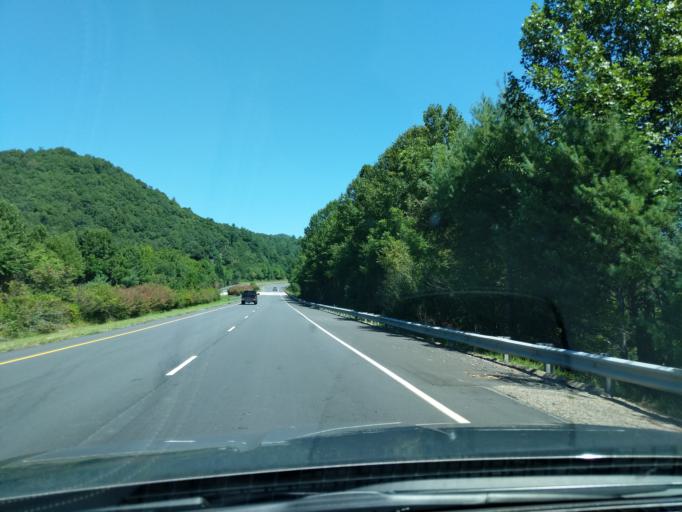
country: US
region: North Carolina
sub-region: Macon County
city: Franklin
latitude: 35.1503
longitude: -83.4666
